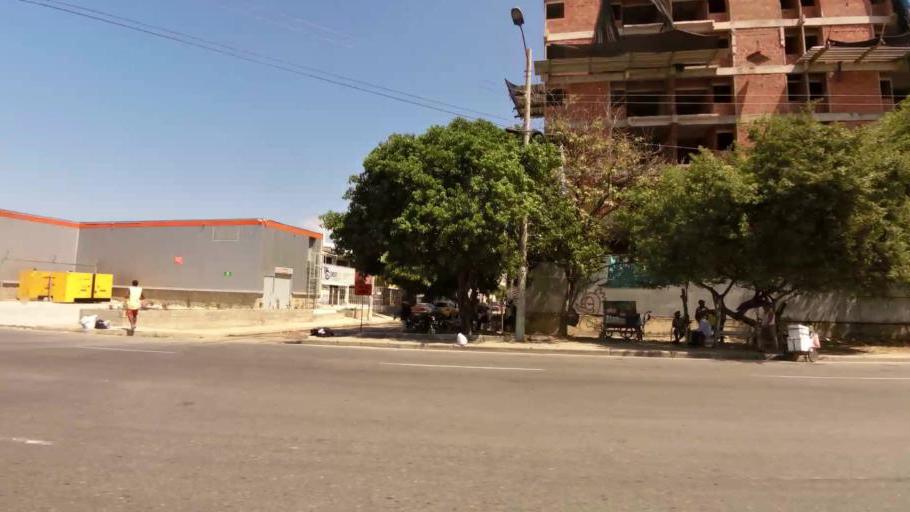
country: CO
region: Bolivar
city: Cartagena
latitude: 10.3874
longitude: -75.5026
